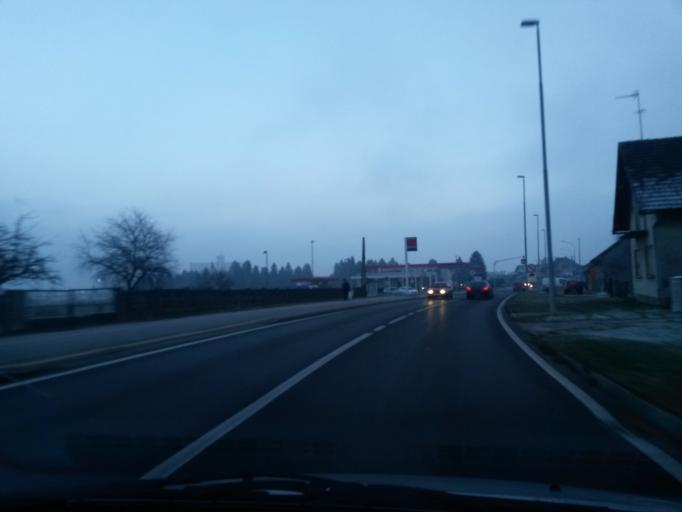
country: HR
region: Koprivnicko-Krizevacka
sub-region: Grad Koprivnica
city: Koprivnica
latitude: 46.1733
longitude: 16.8112
